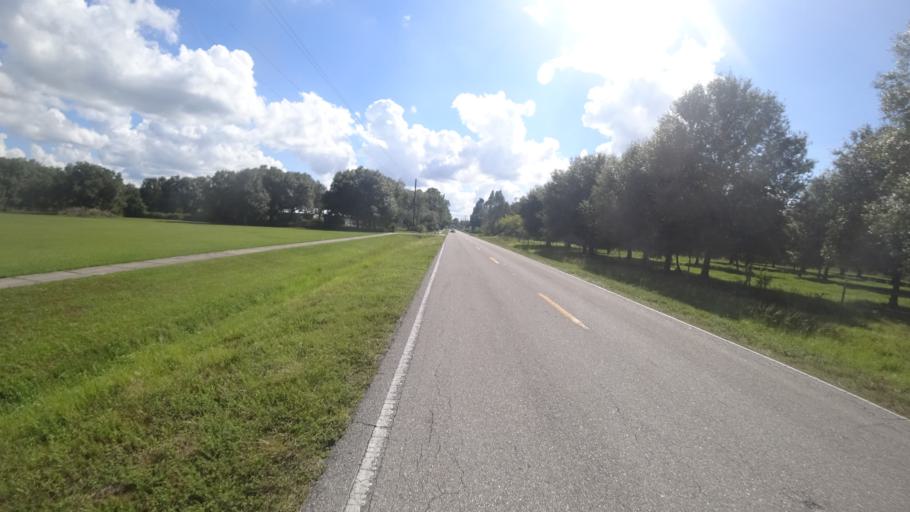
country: US
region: Florida
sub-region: Sarasota County
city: Lake Sarasota
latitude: 27.3543
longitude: -82.1625
